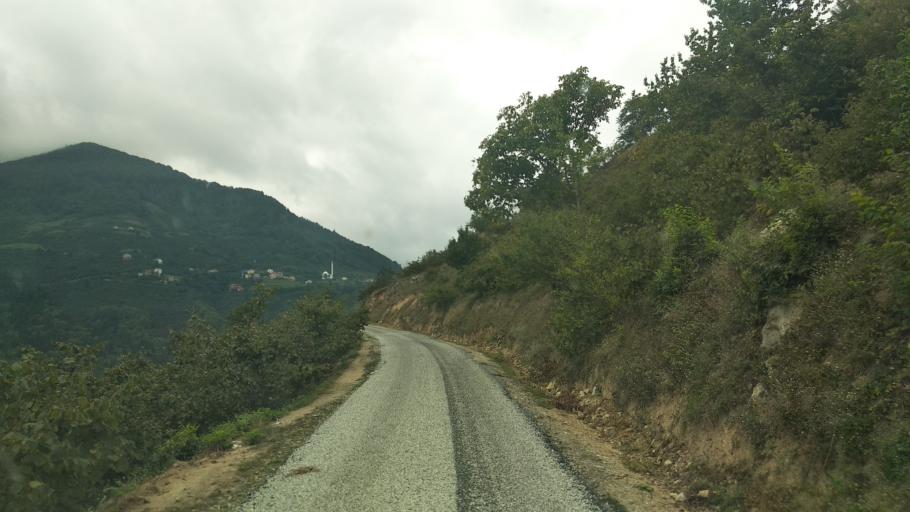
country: TR
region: Giresun
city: Dogankent
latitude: 40.7414
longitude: 38.9916
